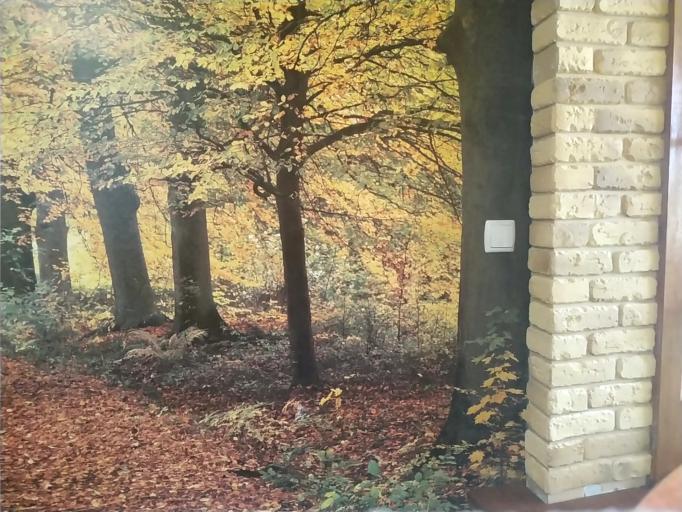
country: RU
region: Tverskaya
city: Vyshniy Volochek
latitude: 57.6471
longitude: 34.5556
